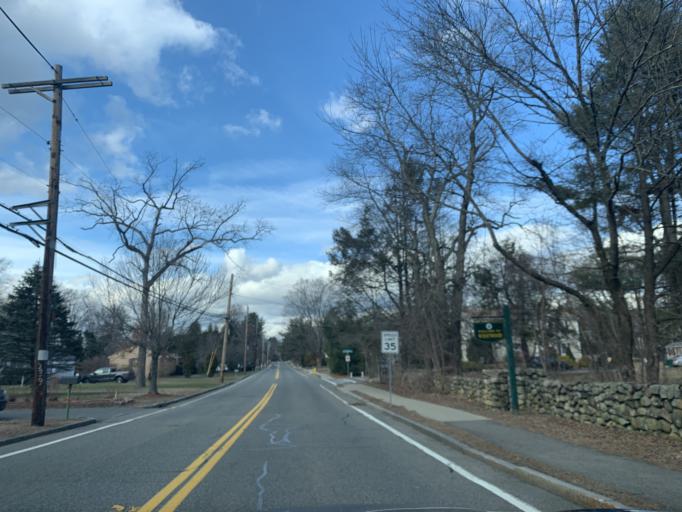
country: US
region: Massachusetts
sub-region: Norfolk County
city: Westwood
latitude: 42.2009
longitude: -71.2188
